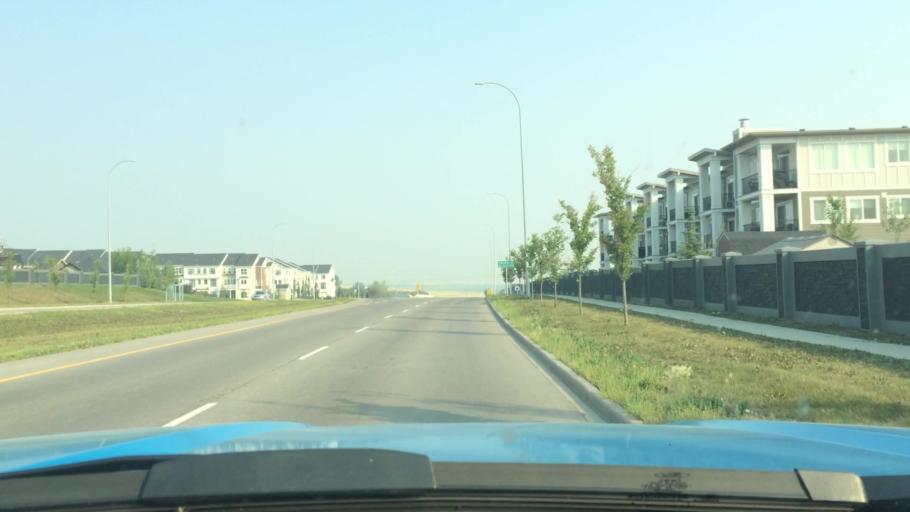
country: CA
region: Alberta
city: Calgary
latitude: 51.1785
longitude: -114.1589
